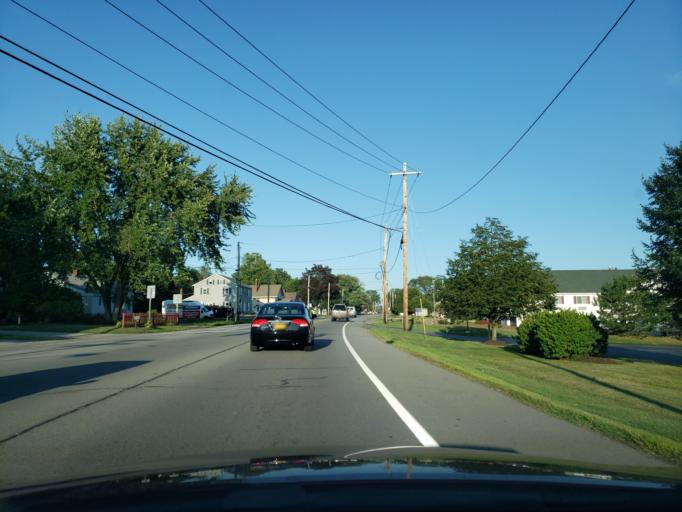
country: US
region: New York
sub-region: Monroe County
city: Webster
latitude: 43.2039
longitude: -77.4923
